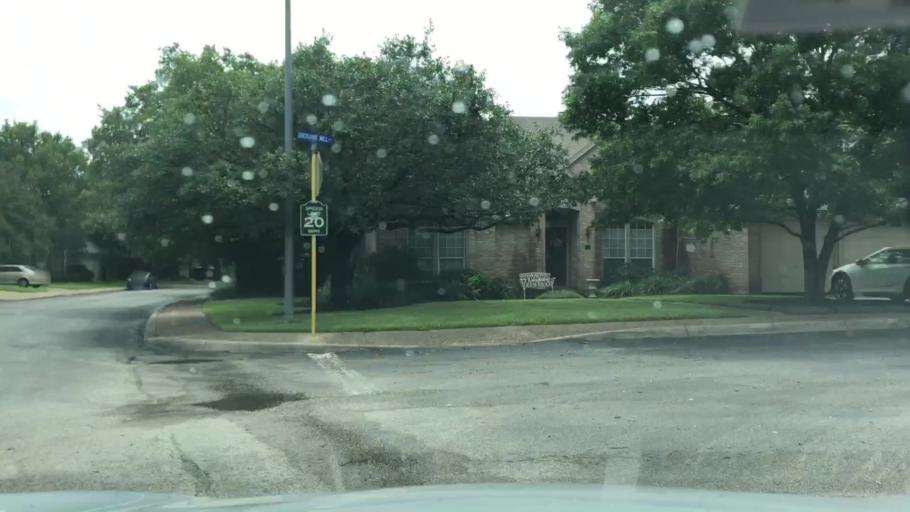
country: US
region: Texas
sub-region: Bexar County
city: Shavano Park
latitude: 29.5969
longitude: -98.5371
